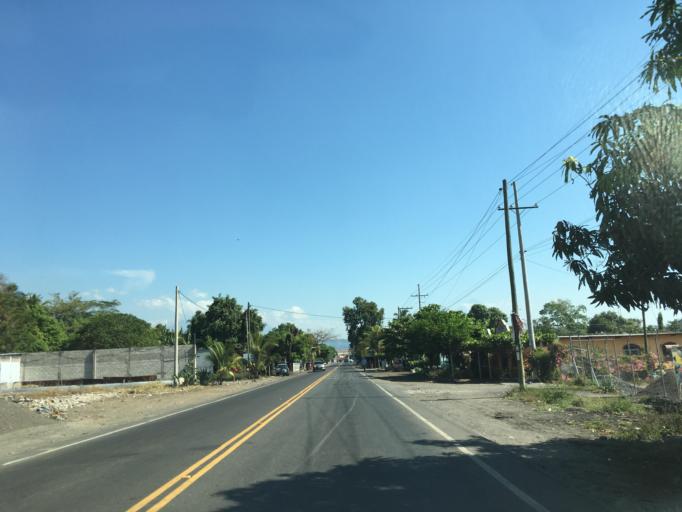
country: GT
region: Escuintla
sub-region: Municipio de La Democracia
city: La Democracia
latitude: 14.2231
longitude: -90.9505
